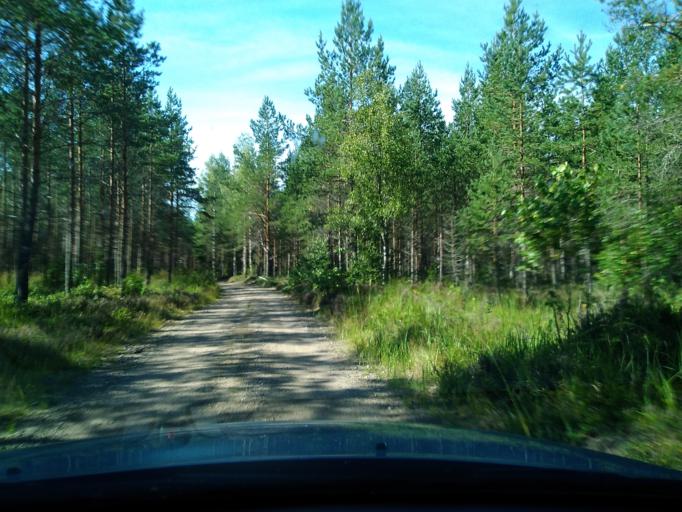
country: FI
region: Uusimaa
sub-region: Helsinki
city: Kaerkoelae
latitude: 60.7281
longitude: 24.0576
